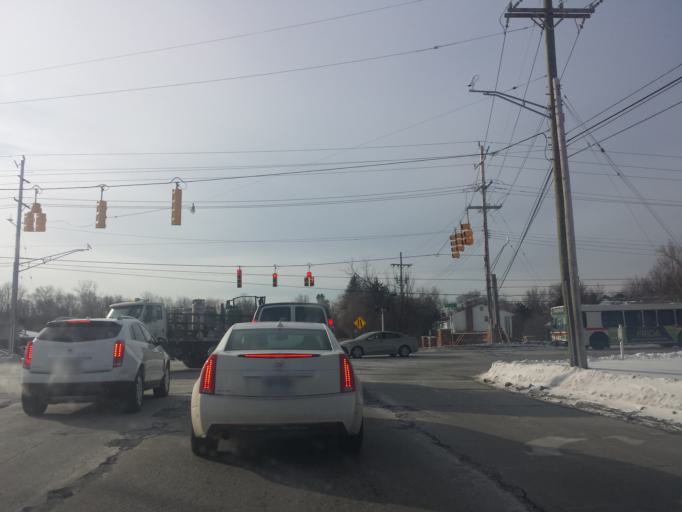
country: US
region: Michigan
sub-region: Oakland County
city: Franklin
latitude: 42.5438
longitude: -83.3412
